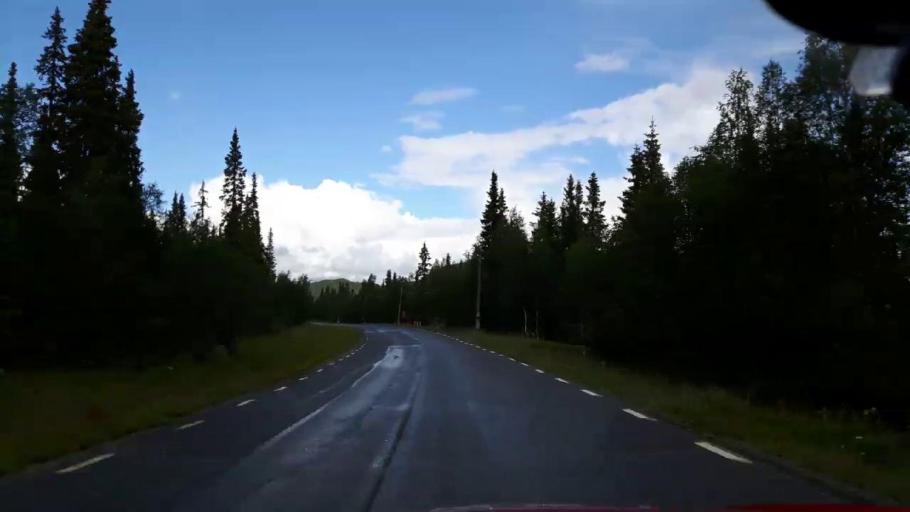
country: SE
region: Vaesterbotten
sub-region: Vilhelmina Kommun
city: Sjoberg
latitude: 65.0192
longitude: 15.1665
